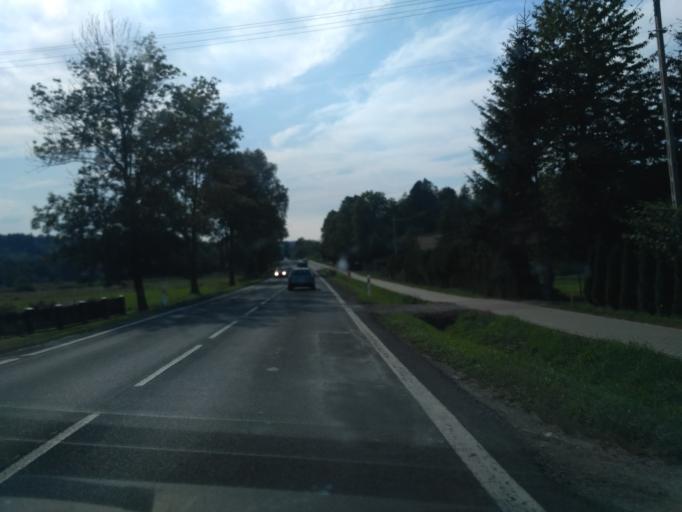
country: PL
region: Subcarpathian Voivodeship
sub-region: Powiat bieszczadzki
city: Ustrzyki Dolne
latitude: 49.4305
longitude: 22.5255
